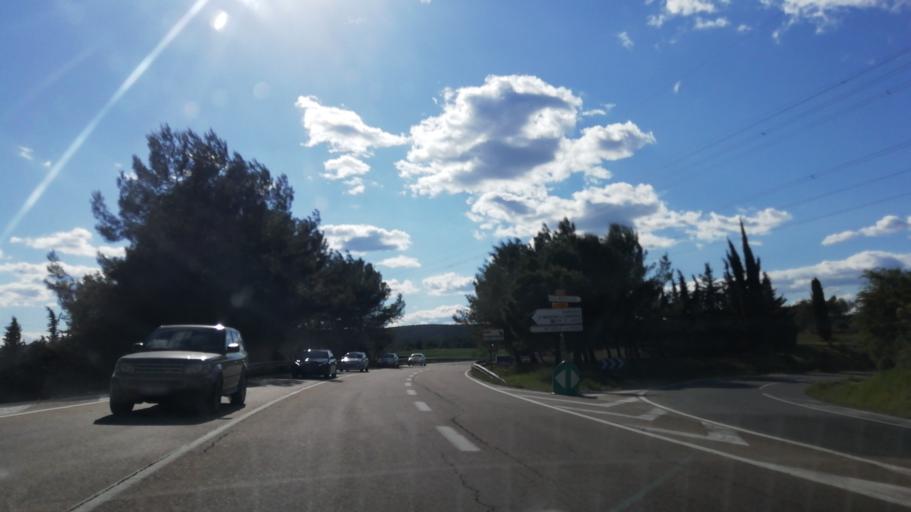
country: FR
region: Languedoc-Roussillon
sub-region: Departement de l'Herault
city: Saint-Gely-du-Fesc
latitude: 43.7072
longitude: 3.8137
